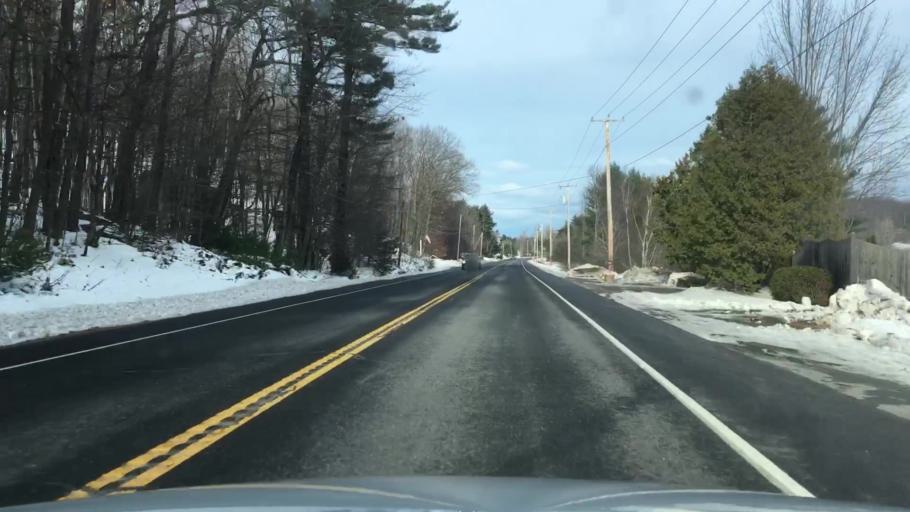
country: US
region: Maine
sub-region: Androscoggin County
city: Greene
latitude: 44.2107
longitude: -70.0984
